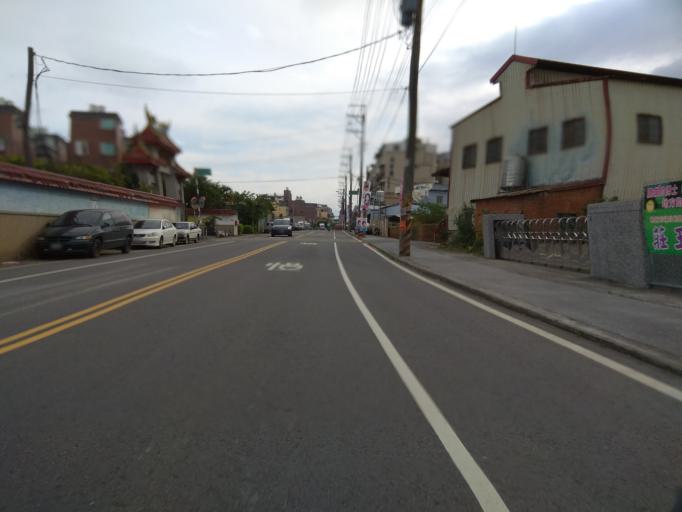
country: TW
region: Taiwan
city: Daxi
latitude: 24.9273
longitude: 121.2059
